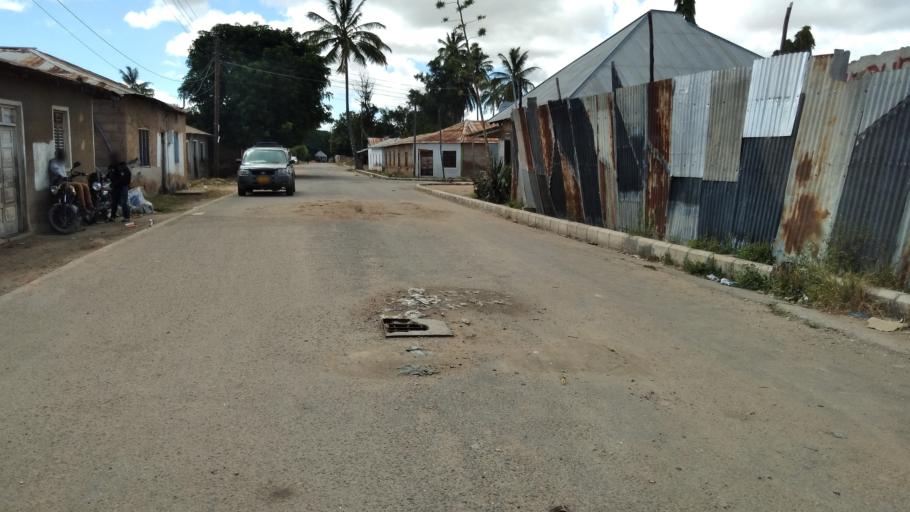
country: TZ
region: Dodoma
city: Dodoma
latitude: -6.1718
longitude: 35.7506
